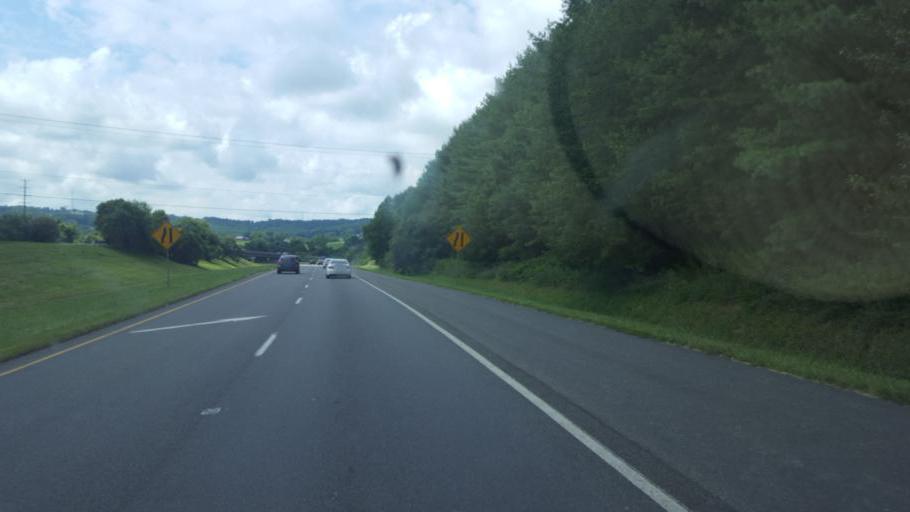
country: US
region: Virginia
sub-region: Fauquier County
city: Warrenton
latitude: 38.7378
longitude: -77.8015
